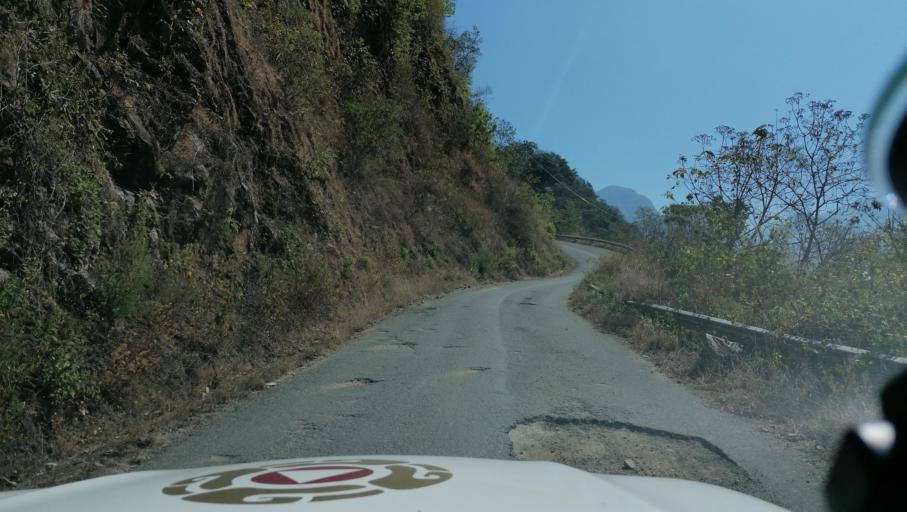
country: MX
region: Chiapas
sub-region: Cacahoatan
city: Benito Juarez
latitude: 15.1845
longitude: -92.1883
